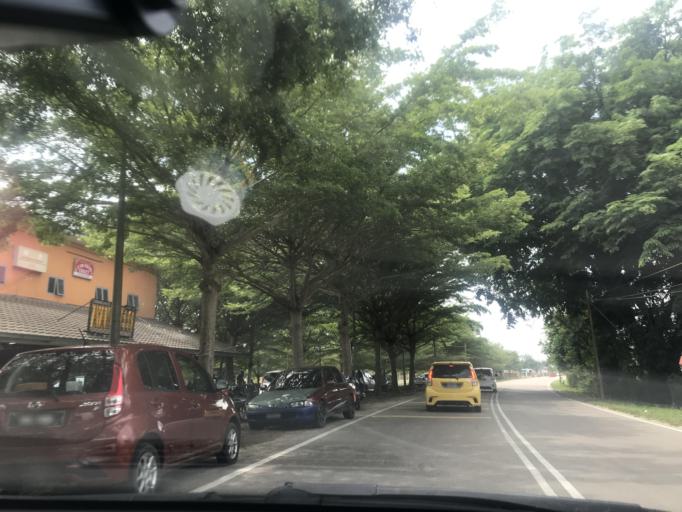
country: MY
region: Kelantan
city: Tumpat
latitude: 6.2180
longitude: 102.1195
